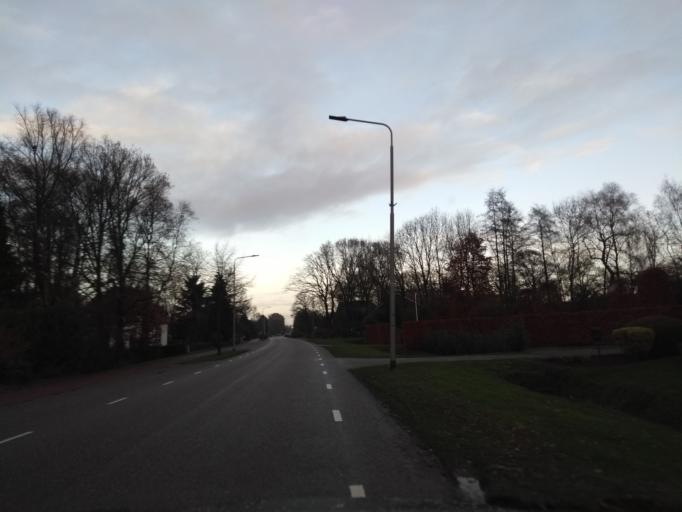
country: NL
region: Overijssel
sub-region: Gemeente Twenterand
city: Westerhaar-Vriezenveensewijk
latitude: 52.4322
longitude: 6.6641
